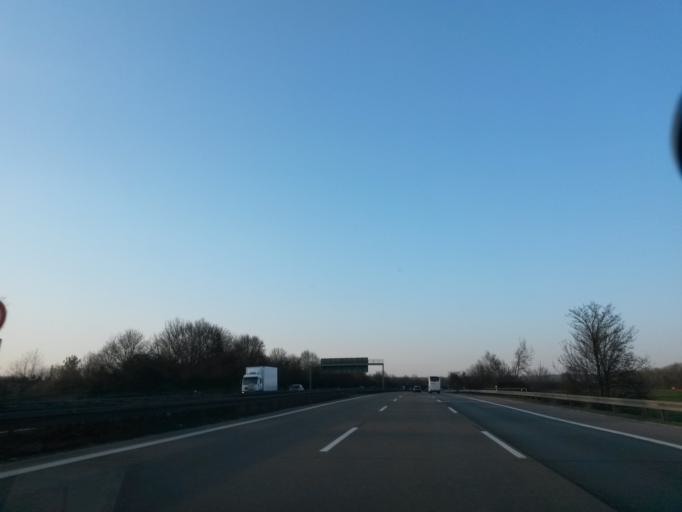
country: DE
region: Bavaria
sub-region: Upper Bavaria
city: Lenting
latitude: 48.7819
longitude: 11.4604
